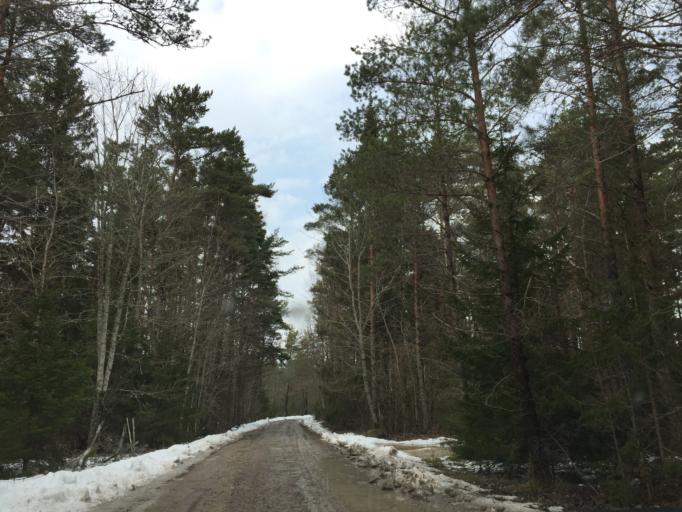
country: EE
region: Saare
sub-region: Kuressaare linn
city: Kuressaare
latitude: 58.4313
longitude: 22.1436
